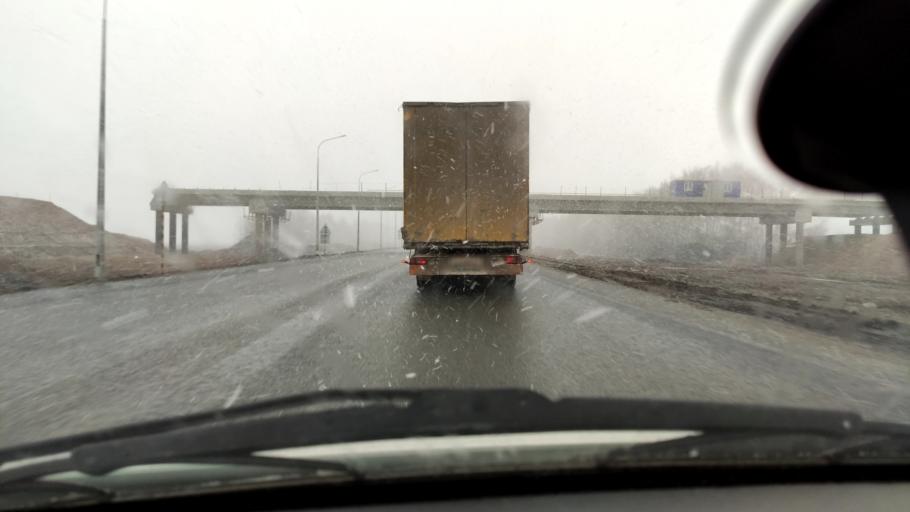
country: RU
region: Bashkortostan
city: Buzdyak
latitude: 54.6579
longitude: 54.6559
